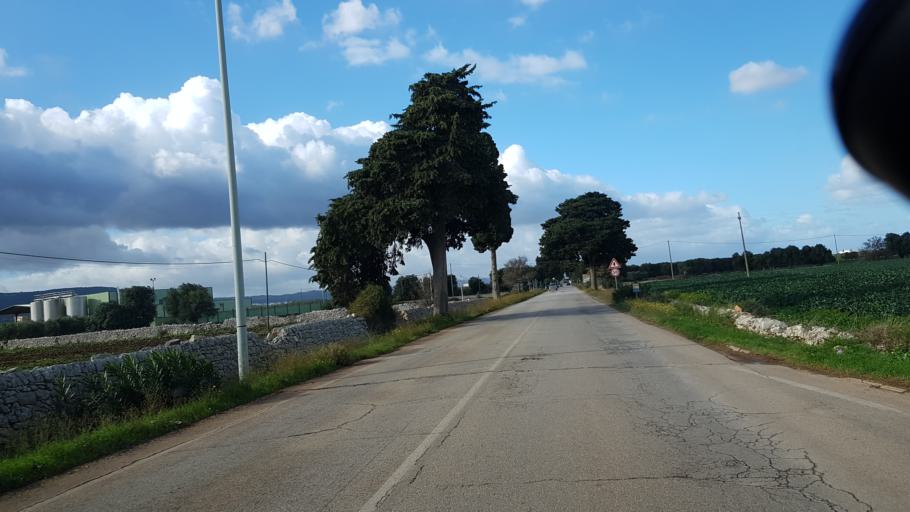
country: IT
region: Apulia
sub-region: Provincia di Brindisi
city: Montalbano
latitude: 40.7869
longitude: 17.4705
